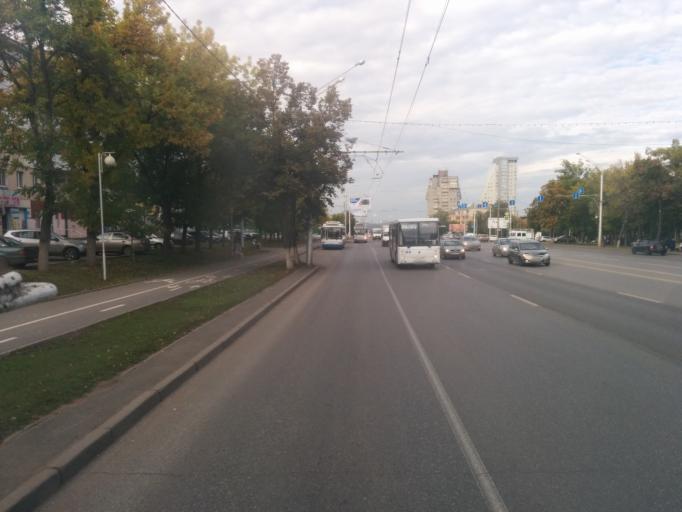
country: RU
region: Bashkortostan
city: Ufa
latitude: 54.7808
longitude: 56.0317
